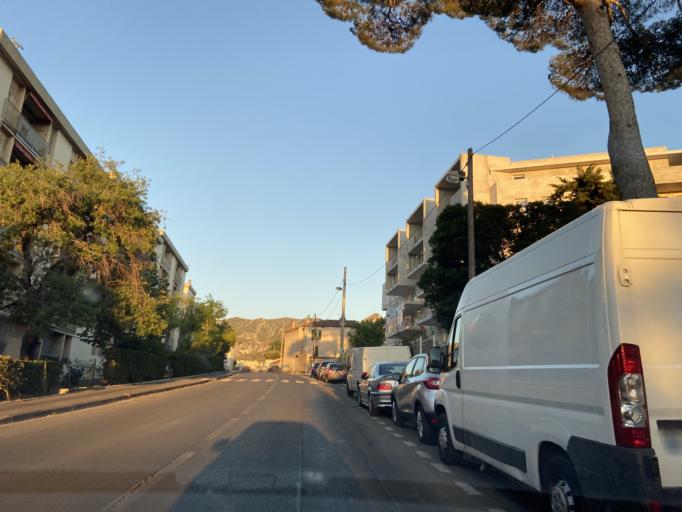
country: FR
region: Provence-Alpes-Cote d'Azur
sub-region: Departement des Bouches-du-Rhone
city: Marseille 10
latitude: 43.2768
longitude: 5.4205
